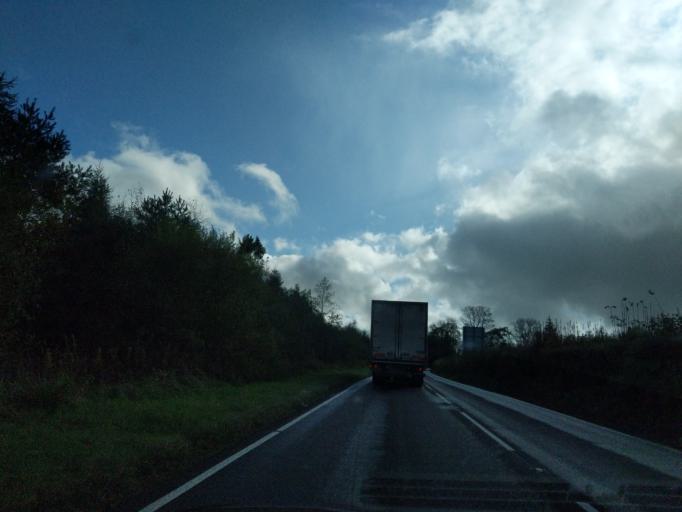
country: GB
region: Scotland
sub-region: Dumfries and Galloway
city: Moffat
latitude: 55.2842
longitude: -3.4445
